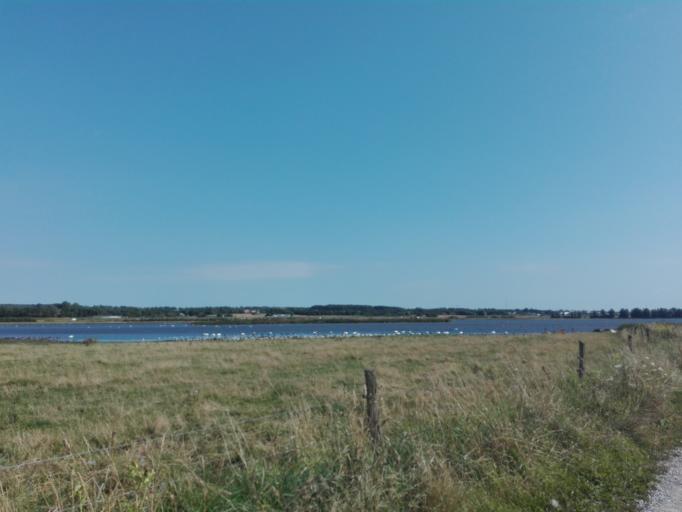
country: DK
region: Central Jutland
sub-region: Arhus Kommune
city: Lystrup
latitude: 56.2139
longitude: 10.2162
